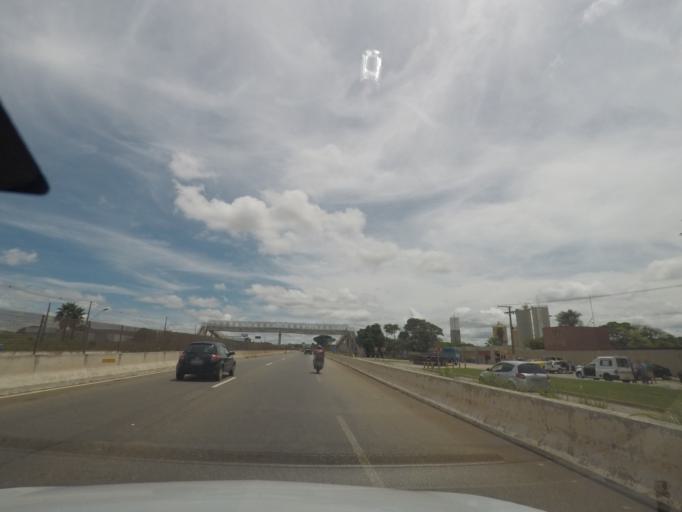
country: BR
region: Goias
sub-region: Goiania
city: Goiania
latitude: -16.7133
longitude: -49.3588
